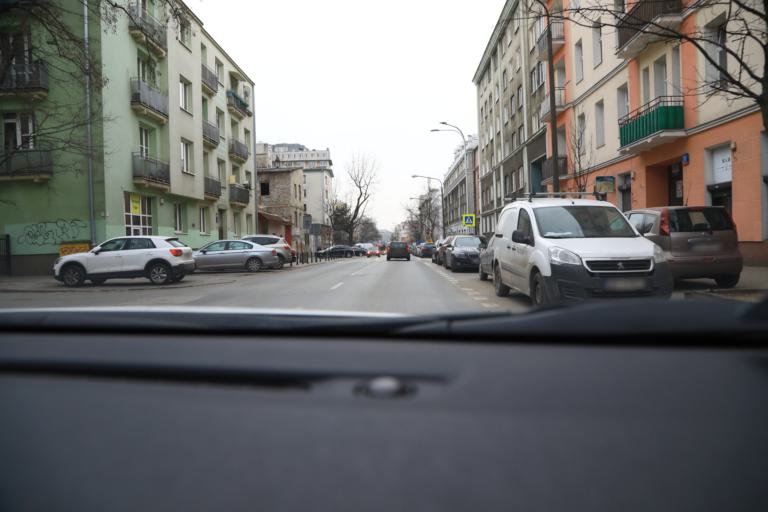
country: PL
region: Masovian Voivodeship
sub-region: Warszawa
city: Wola
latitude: 52.2355
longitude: 20.9654
